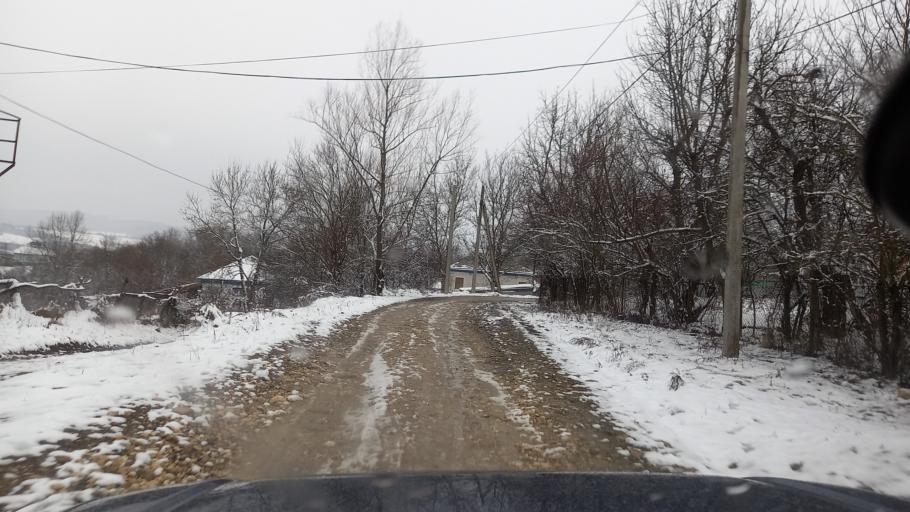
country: RU
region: Adygeya
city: Abadzekhskaya
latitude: 44.3525
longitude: 40.4089
